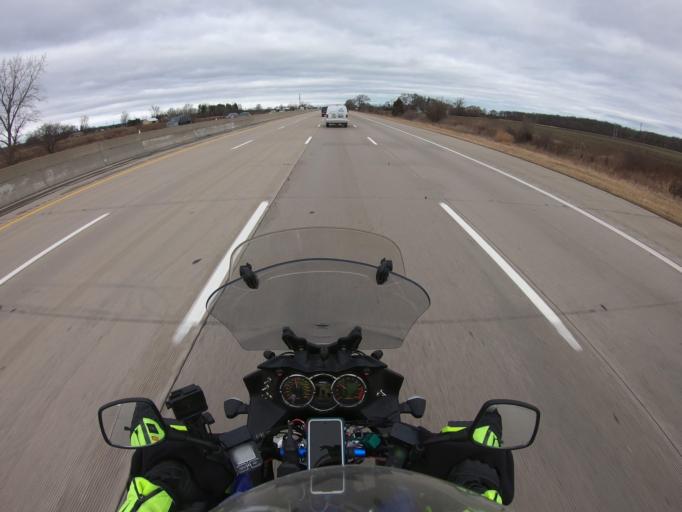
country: US
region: Michigan
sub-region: Saginaw County
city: Zilwaukee
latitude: 43.5420
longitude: -83.9443
